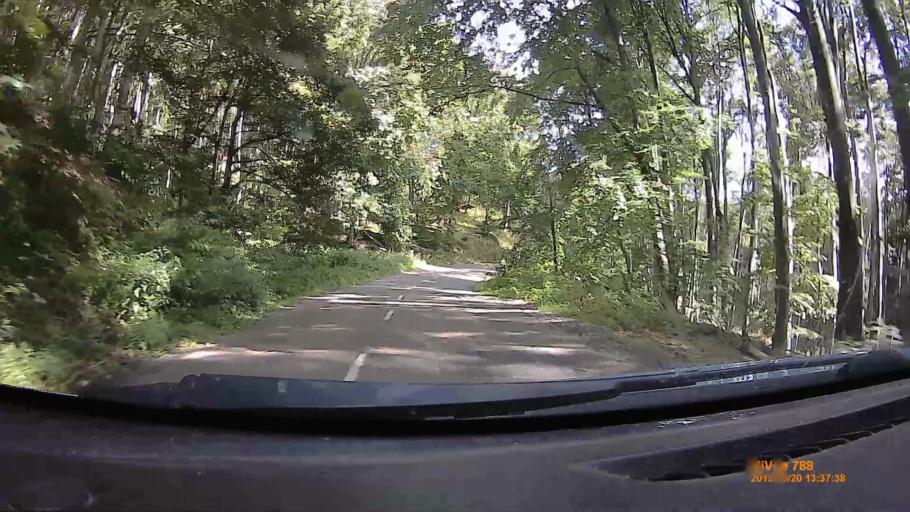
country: HU
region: Heves
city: Szilvasvarad
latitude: 48.0606
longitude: 20.5183
